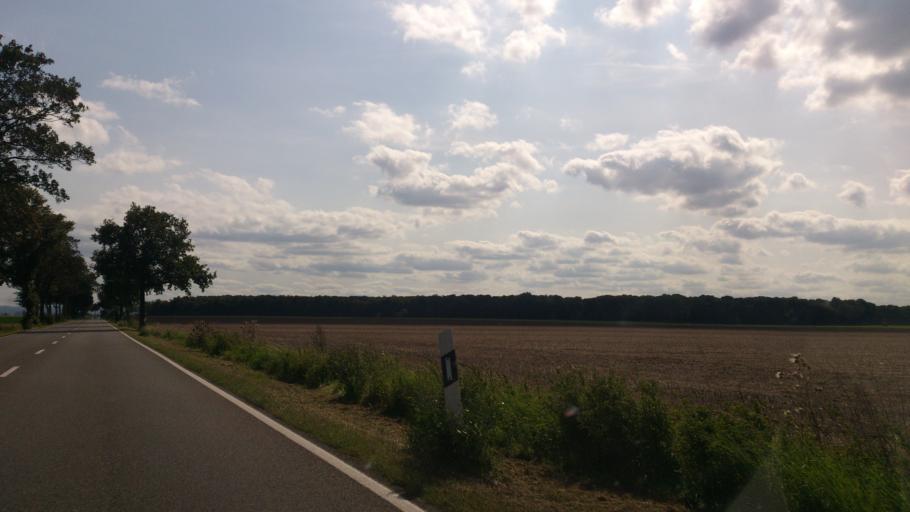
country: DE
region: North Rhine-Westphalia
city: Zulpich
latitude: 50.7384
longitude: 6.7062
